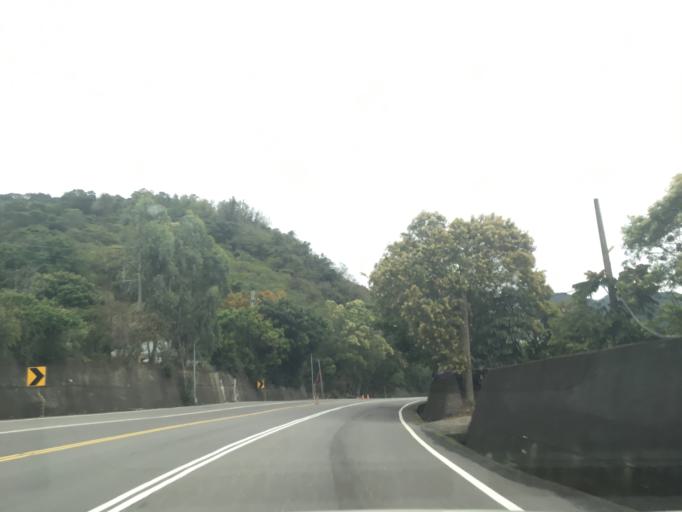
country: TW
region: Taiwan
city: Taitung City
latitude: 22.7493
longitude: 121.0547
